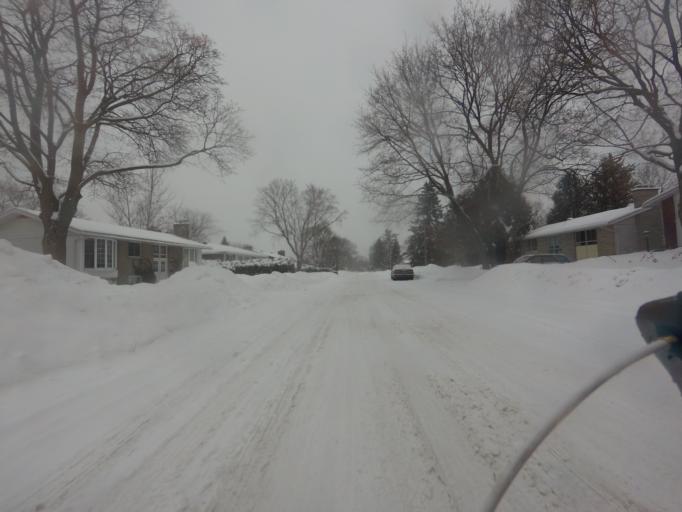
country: CA
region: Ontario
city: Ottawa
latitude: 45.3669
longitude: -75.6792
